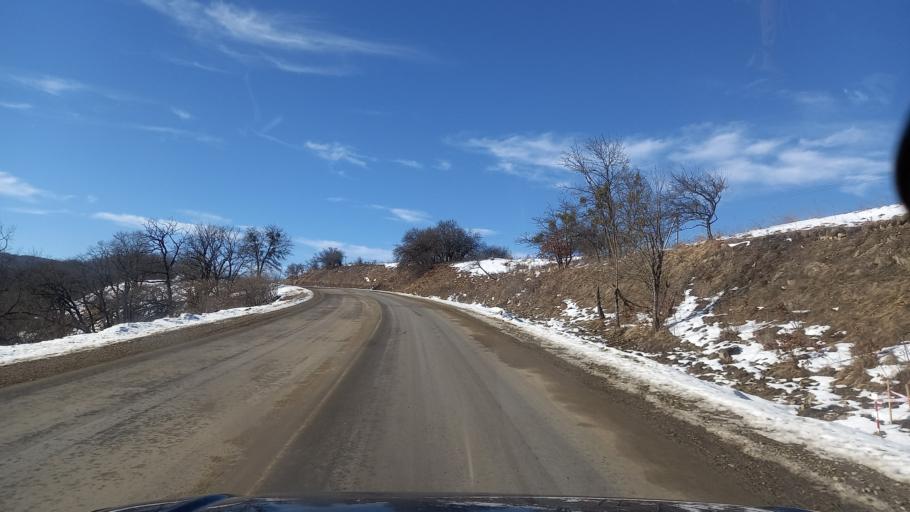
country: RU
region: Adygeya
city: Kamennomostskiy
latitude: 44.2369
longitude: 40.1558
